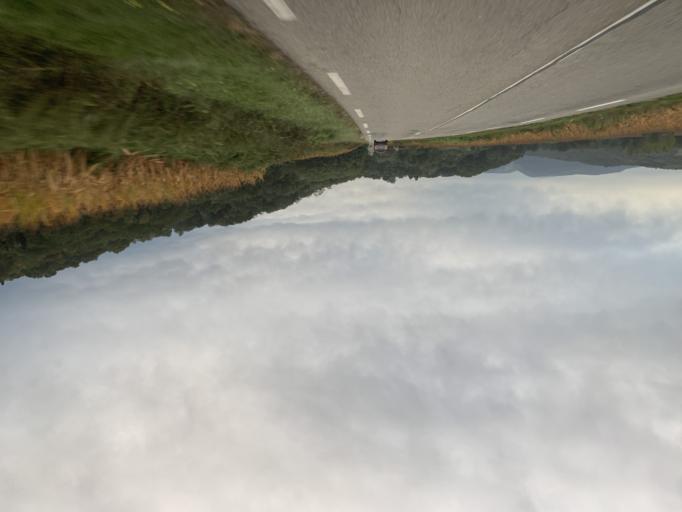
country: FR
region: Rhone-Alpes
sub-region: Departement de l'Ain
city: Belley
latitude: 45.7220
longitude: 5.6653
